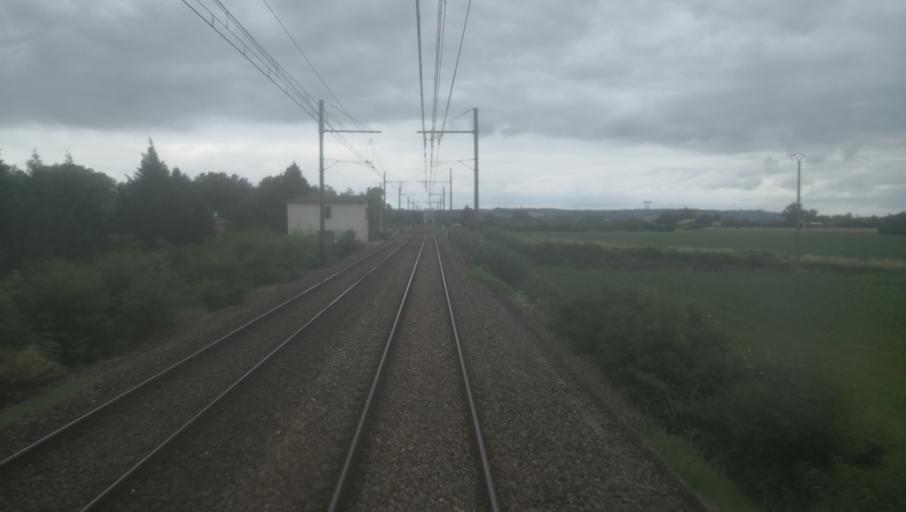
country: FR
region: Midi-Pyrenees
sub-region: Departement du Tarn-et-Garonne
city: Moissac
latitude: 44.0841
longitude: 1.1033
